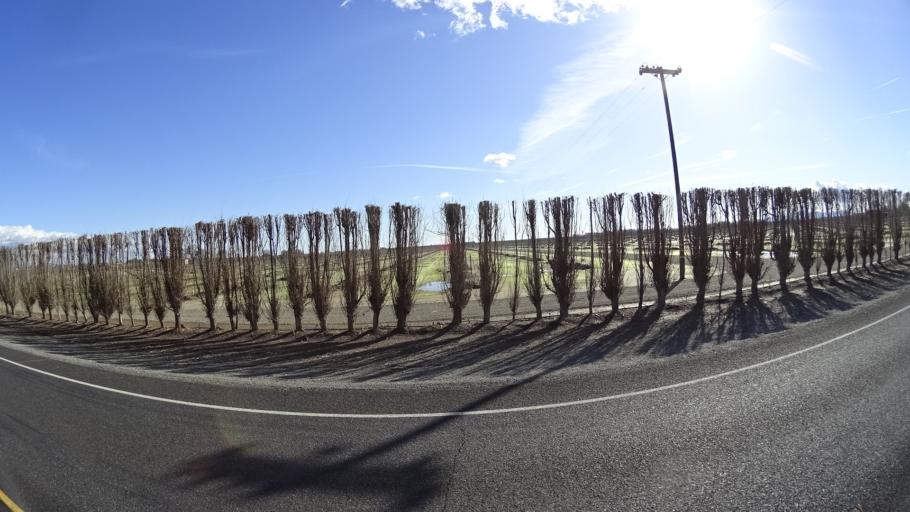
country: US
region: California
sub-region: Butte County
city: Gridley
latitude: 39.3645
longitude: -121.6138
